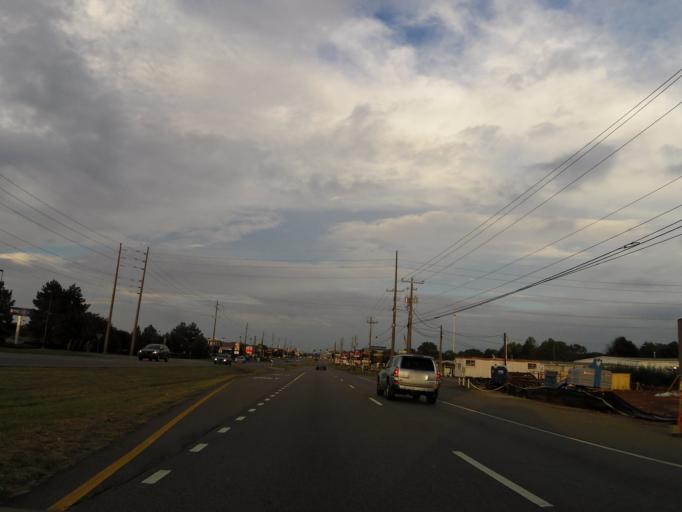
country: US
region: Alabama
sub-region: Madison County
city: Madison
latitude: 34.7527
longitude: -86.7471
